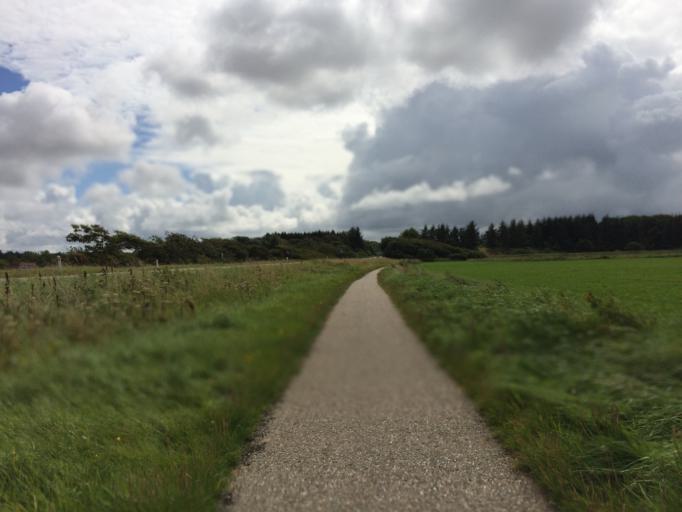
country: DK
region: Central Jutland
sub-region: Holstebro Kommune
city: Ulfborg
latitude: 56.3375
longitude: 8.3456
